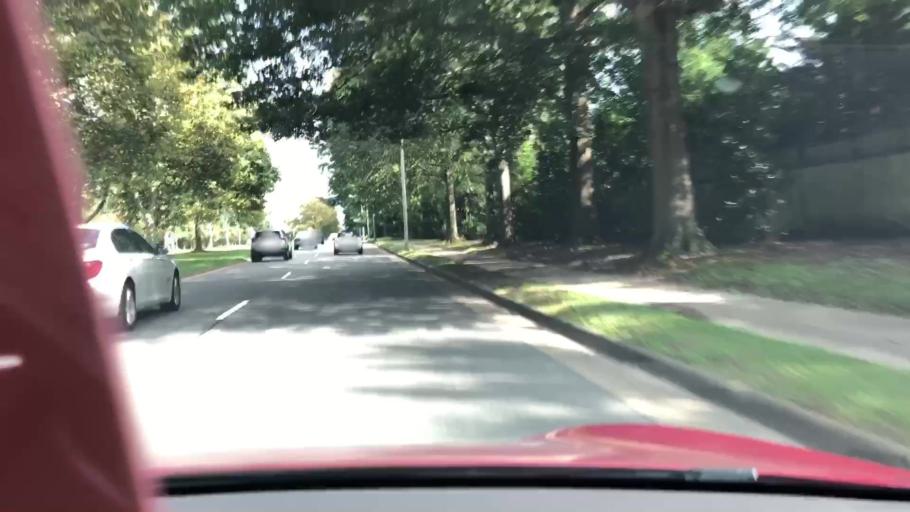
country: US
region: Virginia
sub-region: City of Virginia Beach
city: Virginia Beach
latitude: 36.8926
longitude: -76.0566
